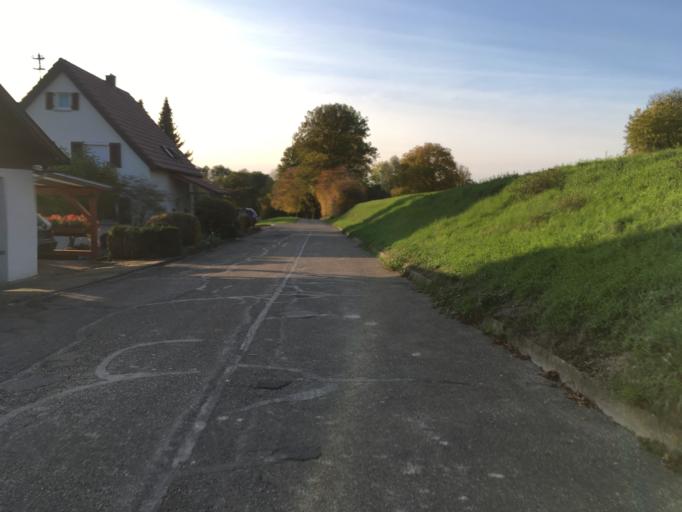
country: DE
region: Baden-Wuerttemberg
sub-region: Regierungsbezirk Stuttgart
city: Neuenstein
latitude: 49.2258
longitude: 9.5628
